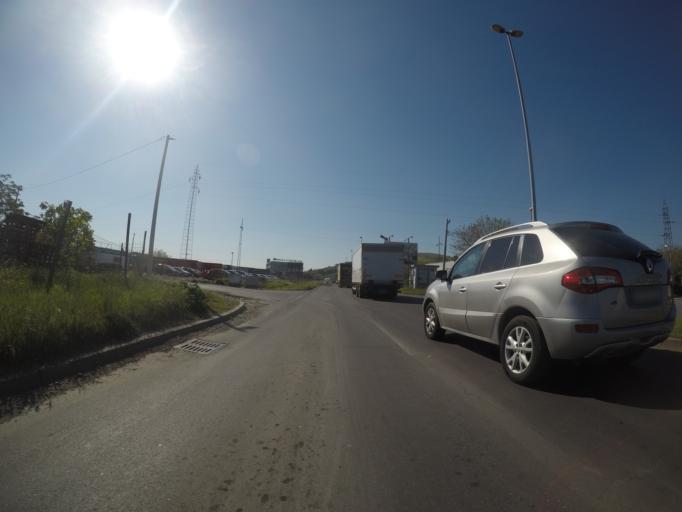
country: ME
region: Podgorica
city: Podgorica
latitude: 42.4285
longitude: 19.2326
